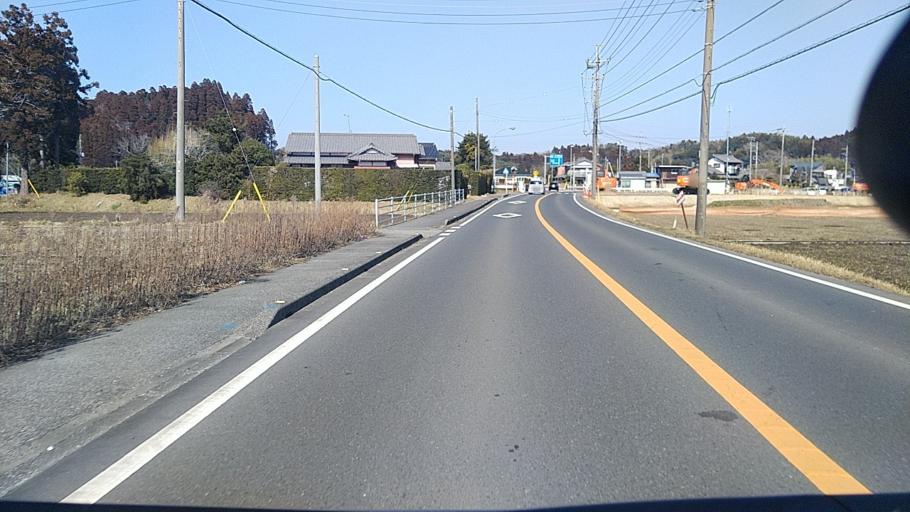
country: JP
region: Chiba
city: Mobara
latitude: 35.4216
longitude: 140.2649
